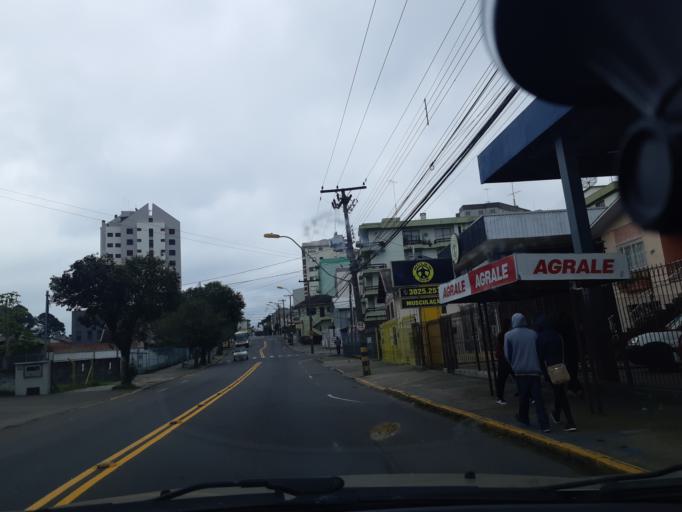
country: BR
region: Rio Grande do Sul
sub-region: Caxias Do Sul
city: Caxias do Sul
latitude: -29.1597
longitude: -51.1947
